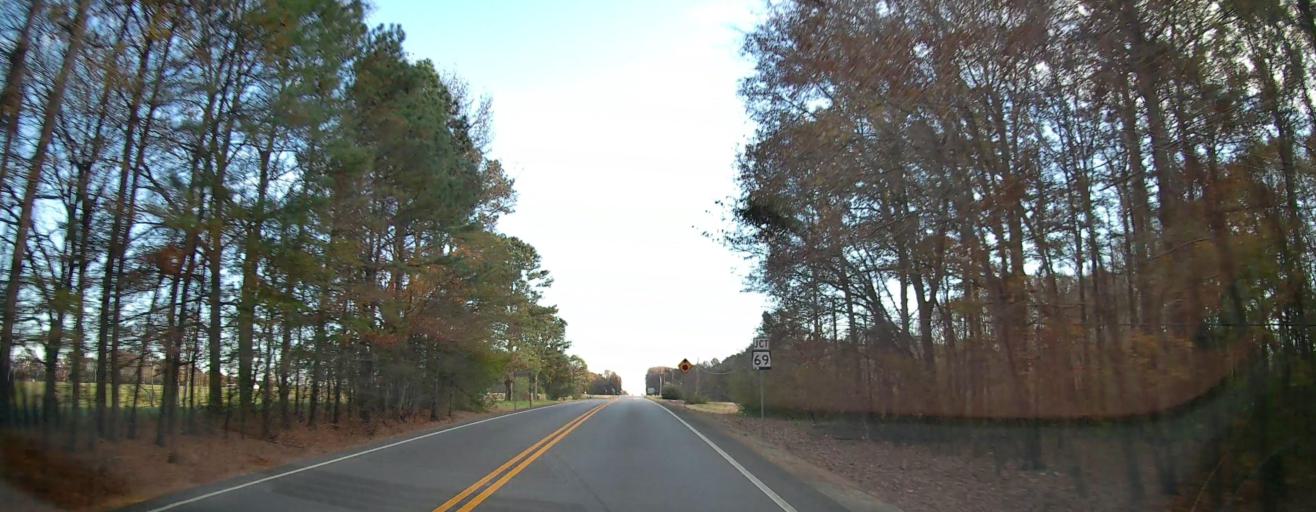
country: US
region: Alabama
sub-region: Marshall County
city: Arab
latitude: 34.2894
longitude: -86.5885
